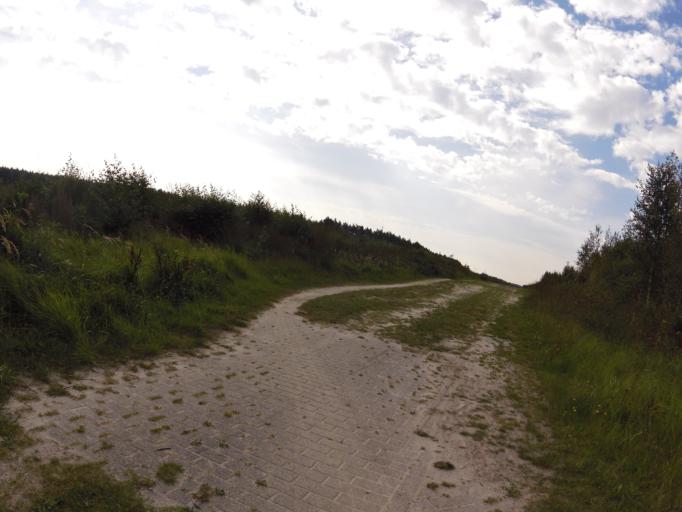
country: DE
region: Lower Saxony
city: Twist
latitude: 52.6995
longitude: 7.0613
